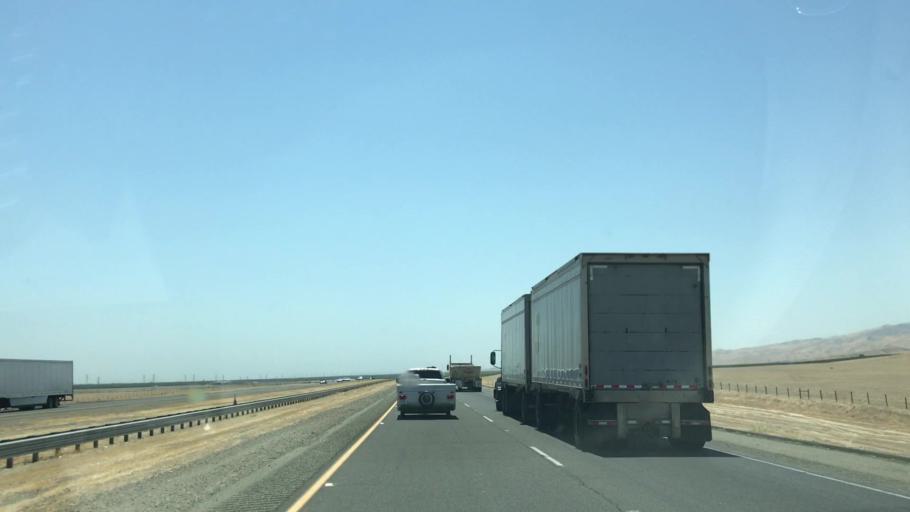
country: US
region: California
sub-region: Fresno County
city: San Joaquin
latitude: 36.4659
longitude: -120.4239
